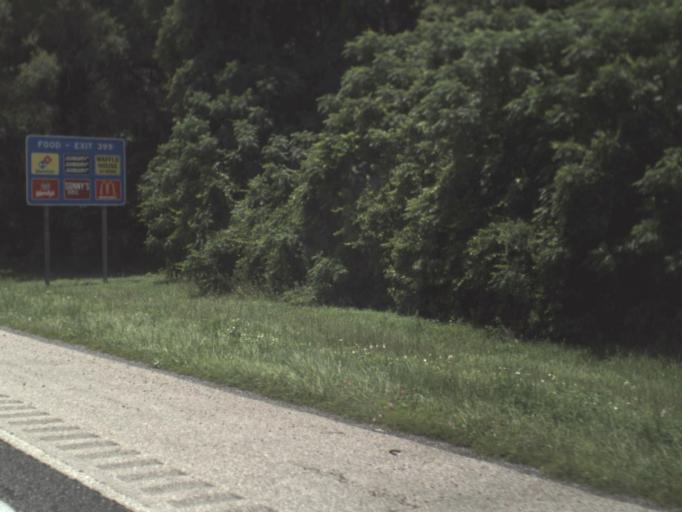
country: US
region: Florida
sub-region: Alachua County
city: High Springs
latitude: 29.8117
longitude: -82.5136
